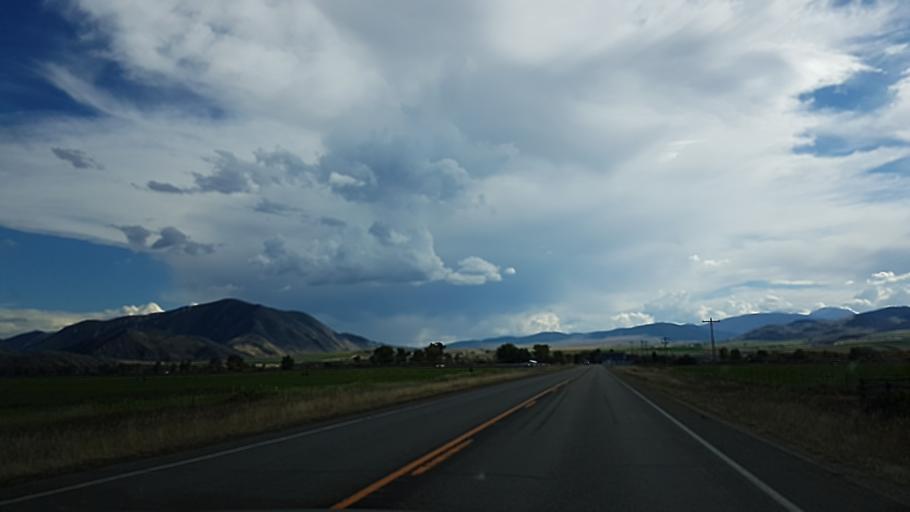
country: US
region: Montana
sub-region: Jefferson County
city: Whitehall
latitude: 45.8651
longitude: -111.9537
